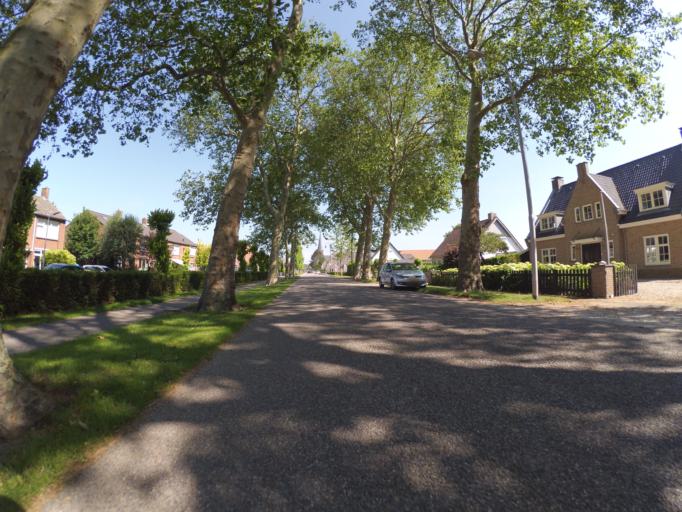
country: NL
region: Utrecht
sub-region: Gemeente IJsselstein
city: IJsselstein
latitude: 51.9606
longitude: 5.0371
